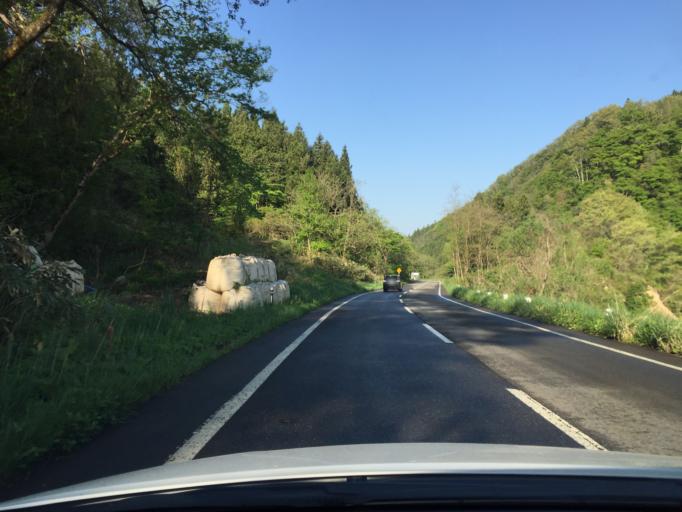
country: JP
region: Fukushima
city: Kitakata
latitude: 37.6650
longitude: 139.9664
